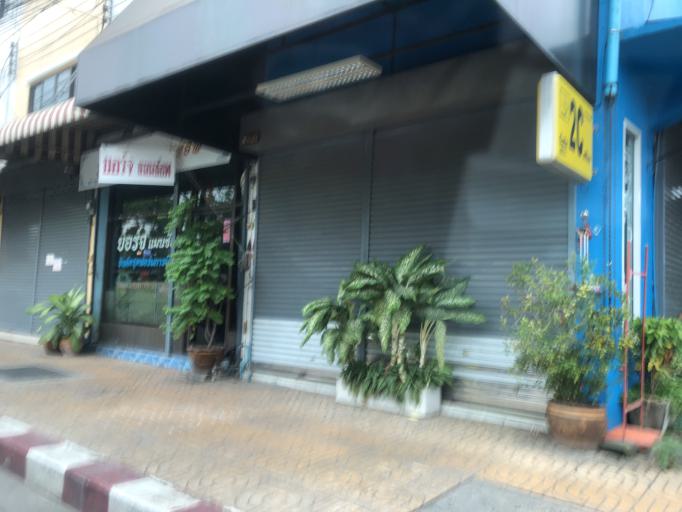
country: TH
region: Bangkok
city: Don Mueang
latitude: 13.9237
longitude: 100.5998
